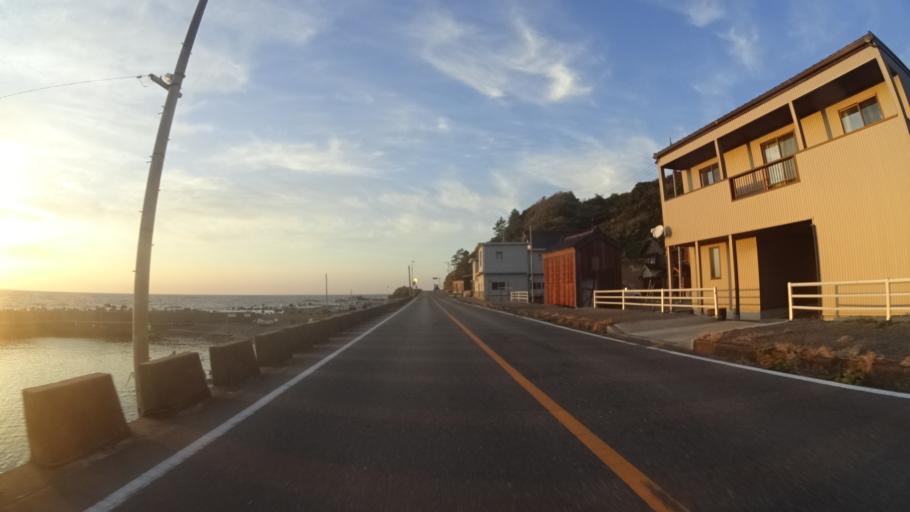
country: JP
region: Ishikawa
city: Nanao
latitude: 37.2334
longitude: 136.7041
